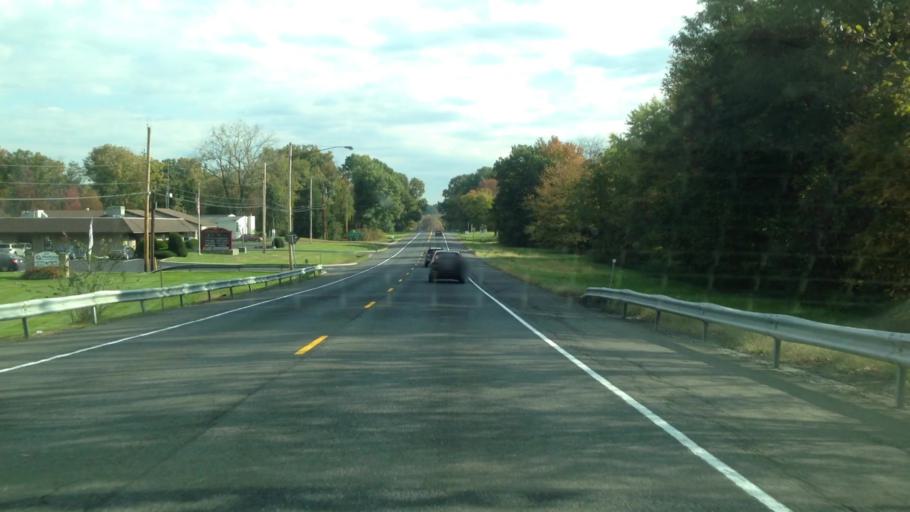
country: US
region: New York
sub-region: Ulster County
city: Highland
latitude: 41.7423
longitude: -73.9964
